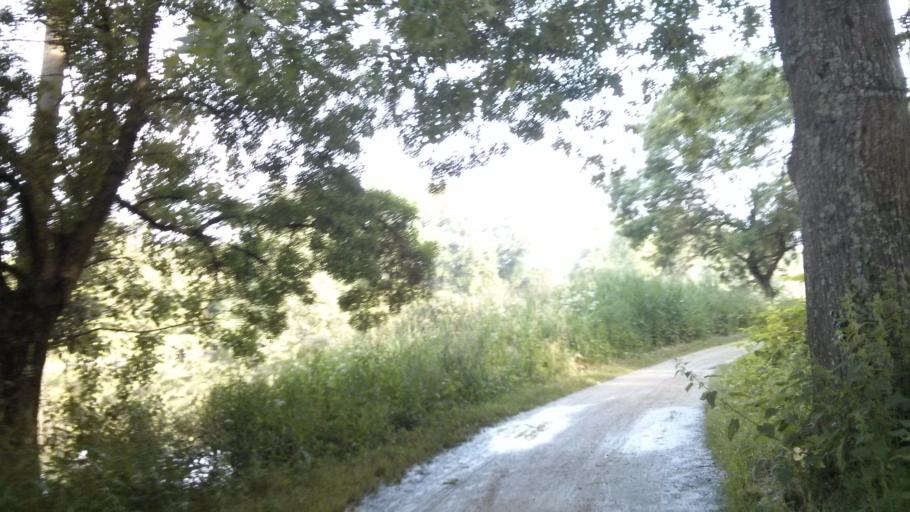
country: FR
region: Pays de la Loire
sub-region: Departement de la Loire-Atlantique
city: Reze
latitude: 47.1863
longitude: -1.5343
